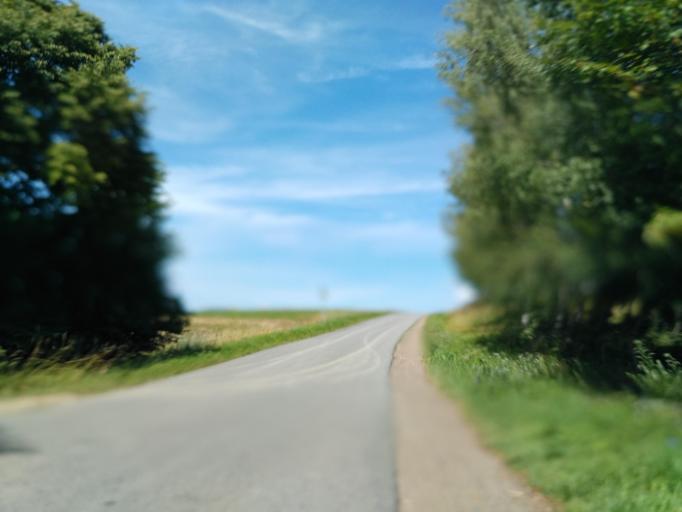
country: PL
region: Subcarpathian Voivodeship
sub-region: Powiat sanocki
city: Strachocina
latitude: 49.5859
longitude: 22.1287
